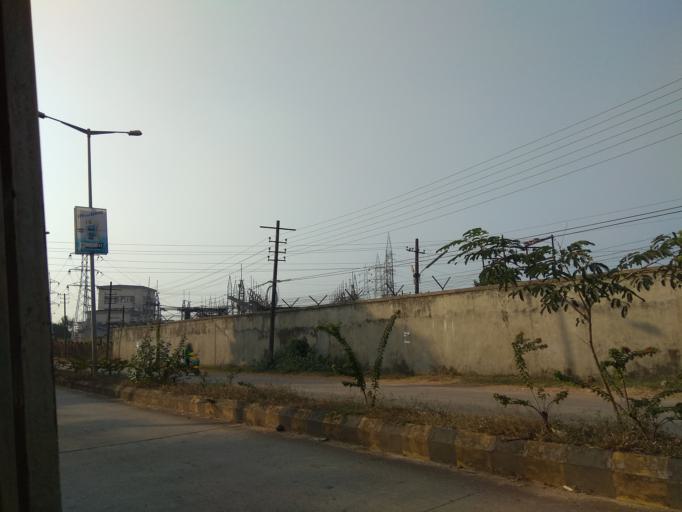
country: IN
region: Karnataka
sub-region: Dakshina Kannada
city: Mangalore
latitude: 12.9242
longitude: 74.8635
